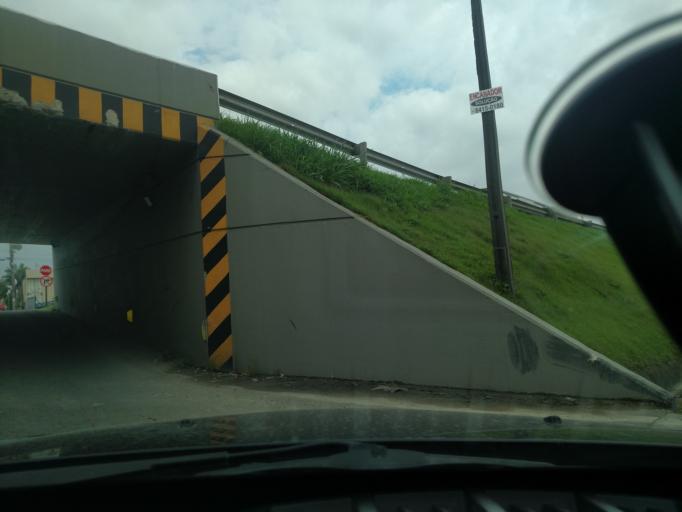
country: BR
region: Santa Catarina
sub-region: Itajai
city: Itajai
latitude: -26.8696
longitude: -48.7296
